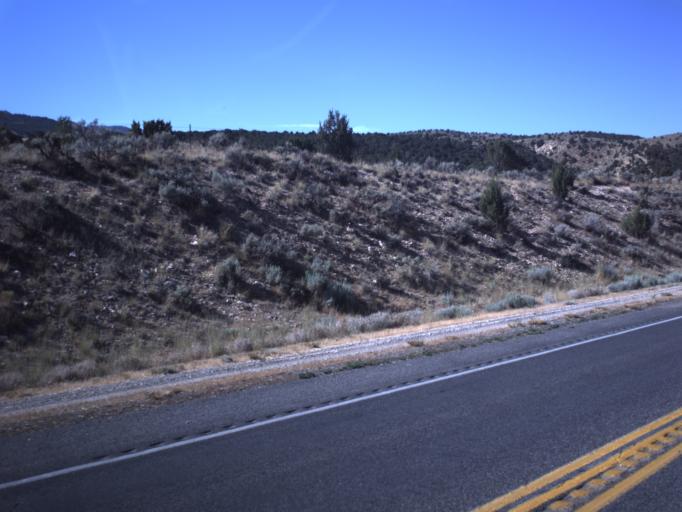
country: US
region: Utah
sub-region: Sanpete County
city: Manti
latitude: 39.2478
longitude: -111.6468
